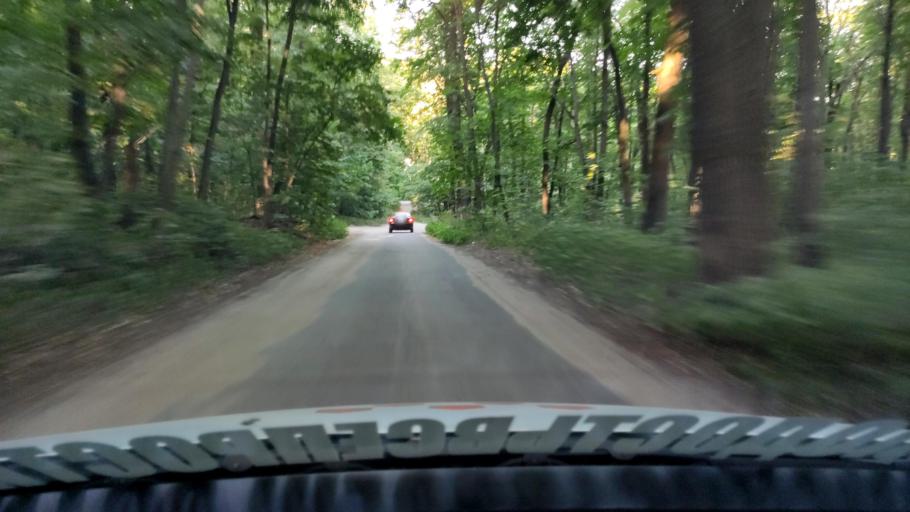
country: RU
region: Voronezj
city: Podgornoye
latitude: 51.7432
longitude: 39.2223
